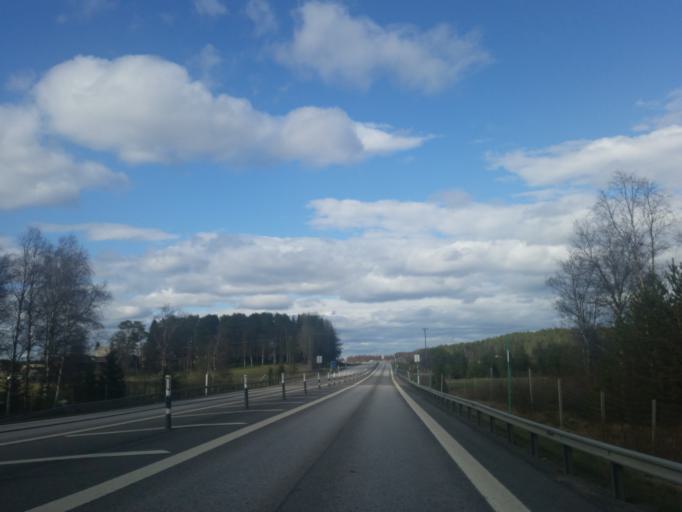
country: SE
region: Vaesterbotten
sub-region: Robertsfors Kommun
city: Robertsfors
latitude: 64.1293
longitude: 20.8888
